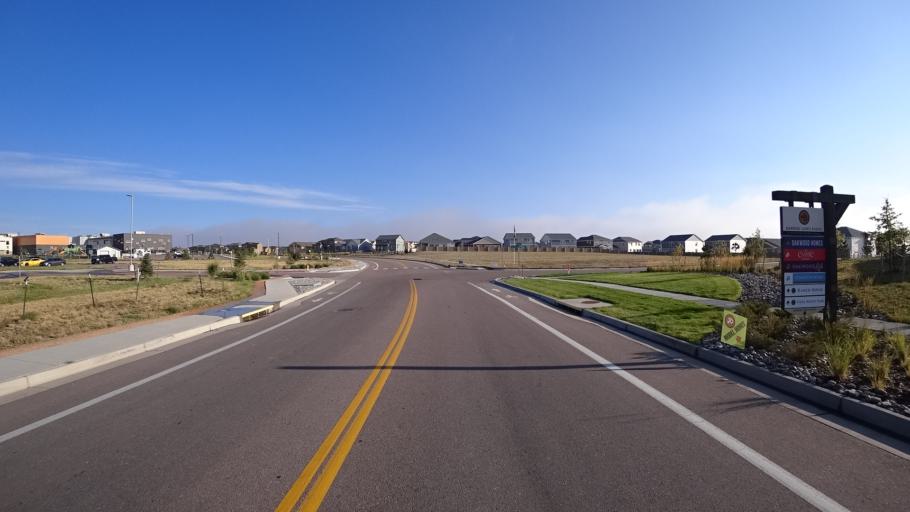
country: US
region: Colorado
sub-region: El Paso County
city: Cimarron Hills
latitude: 38.9312
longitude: -104.6577
